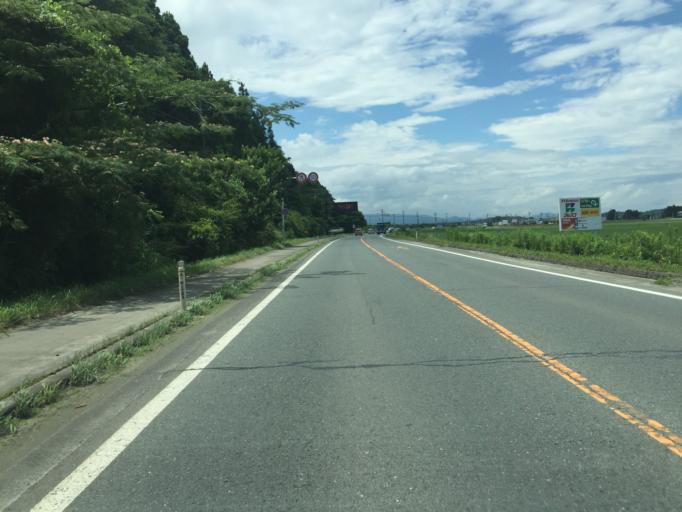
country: JP
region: Fukushima
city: Namie
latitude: 37.6879
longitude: 140.9787
